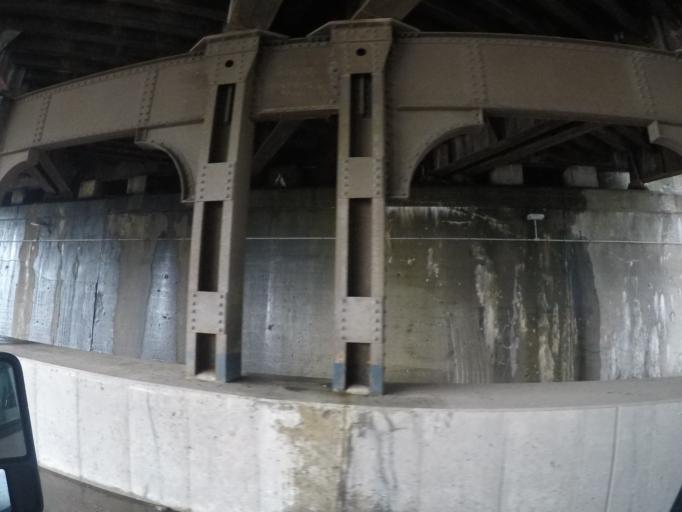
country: US
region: Michigan
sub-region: Wayne County
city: River Rouge
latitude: 42.3184
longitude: -83.1113
